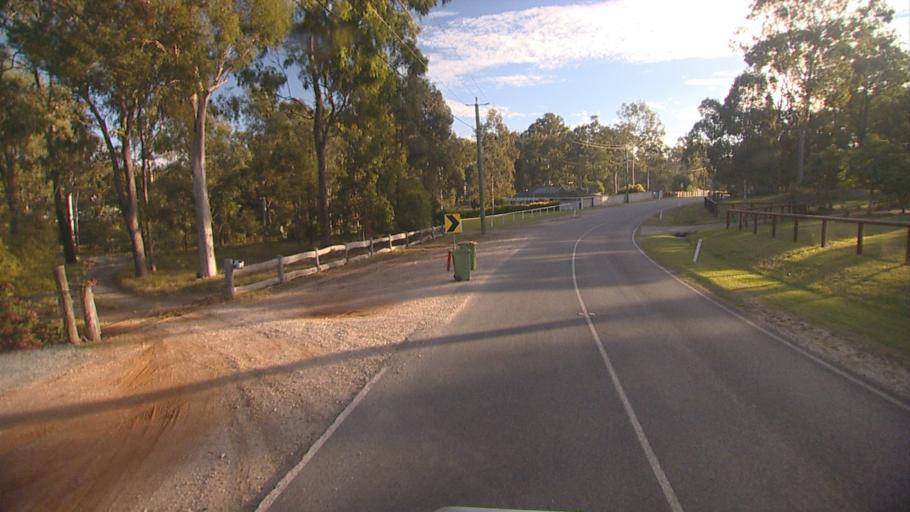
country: AU
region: Queensland
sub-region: Logan
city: Waterford West
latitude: -27.7328
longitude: 153.1402
